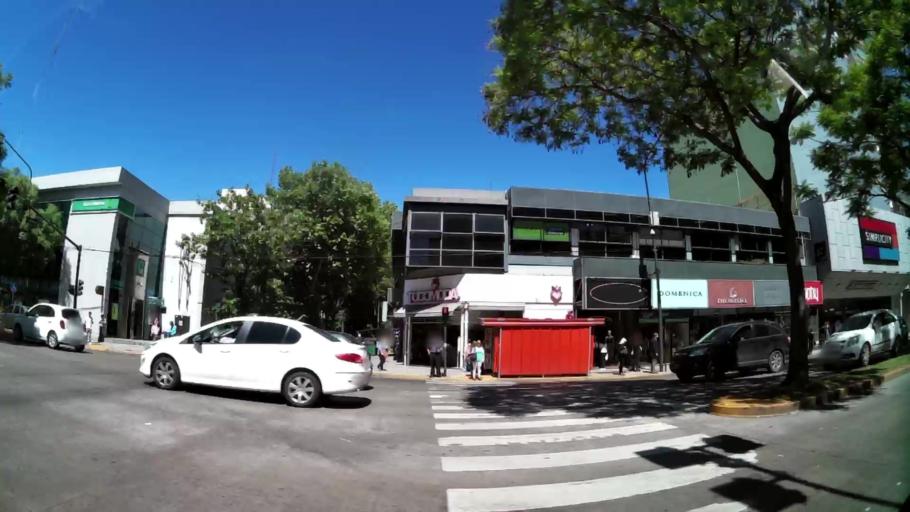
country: AR
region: Buenos Aires
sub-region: Partido de Vicente Lopez
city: Olivos
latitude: -34.5113
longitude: -58.4904
